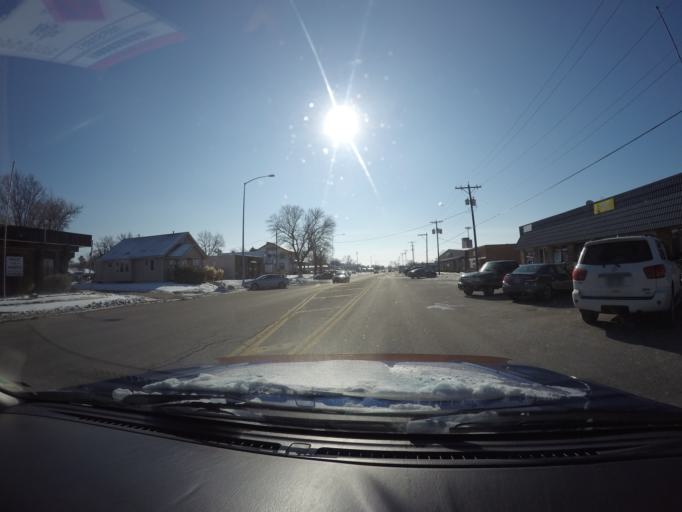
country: US
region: Kansas
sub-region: Johnson County
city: Olathe
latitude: 38.8801
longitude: -94.8207
